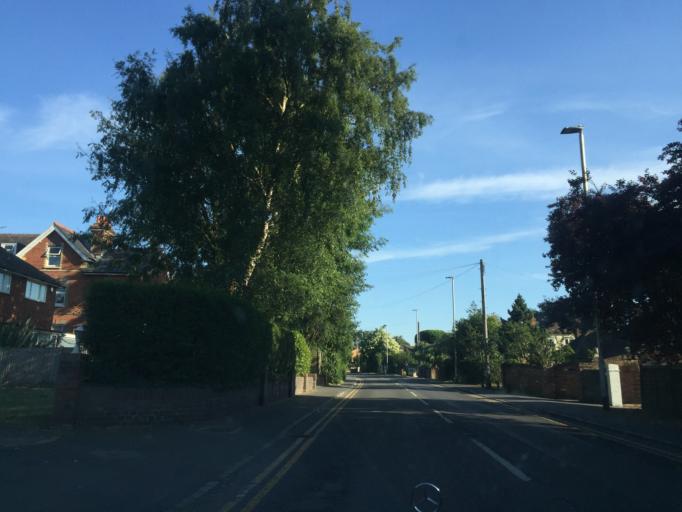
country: GB
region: England
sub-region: Wokingham
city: Twyford
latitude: 51.4807
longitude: -0.8689
